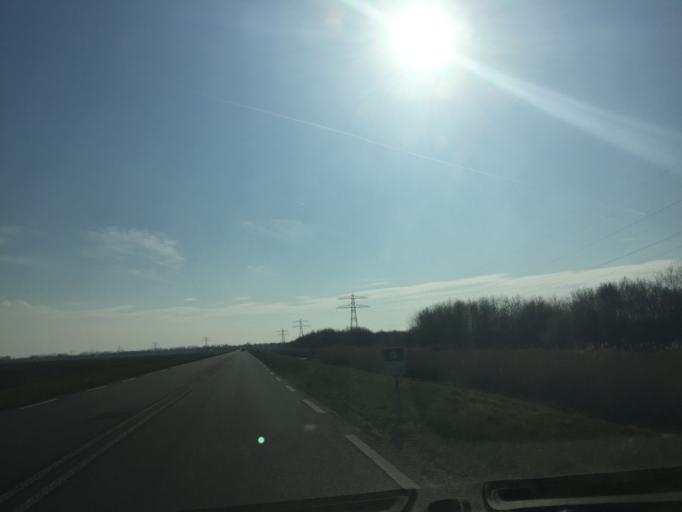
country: NL
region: South Holland
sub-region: Gemeente Hillegom
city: Hillegom
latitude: 52.2790
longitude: 4.5972
